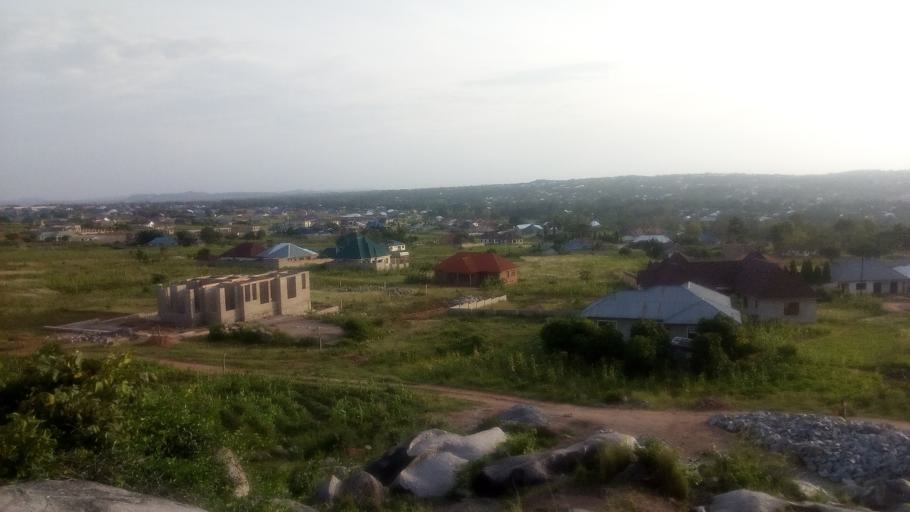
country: TZ
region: Mwanza
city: Mwanza
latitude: -2.4952
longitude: 32.9717
